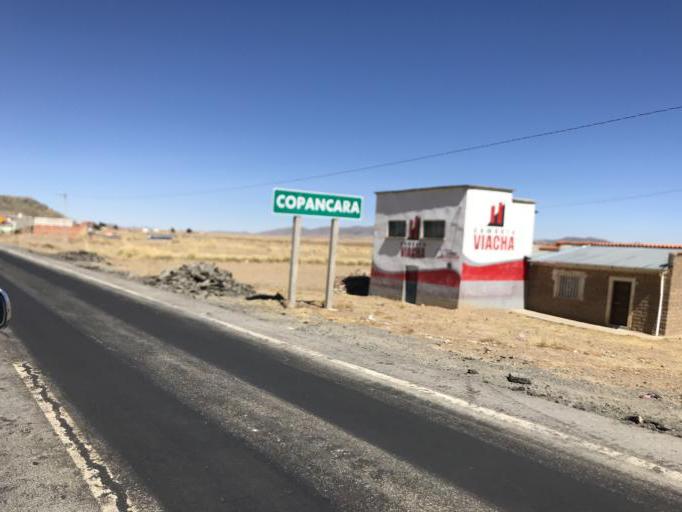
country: BO
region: La Paz
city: Batallas
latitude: -16.2429
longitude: -68.5733
